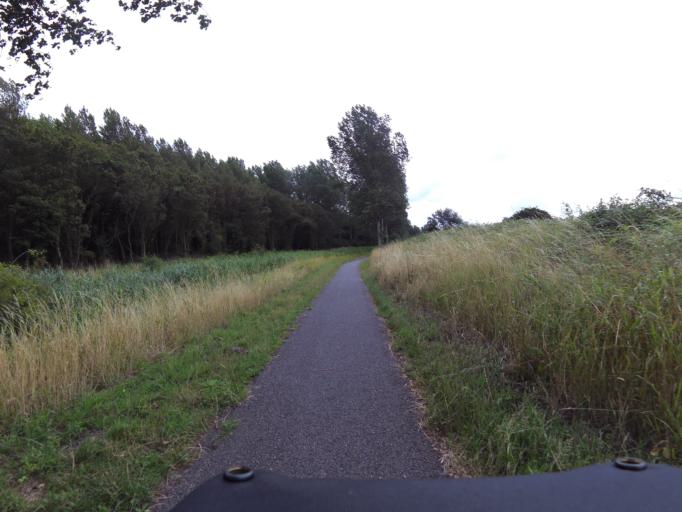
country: NL
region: South Holland
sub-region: Gemeente Goeree-Overflakkee
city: Goedereede
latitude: 51.8315
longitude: 4.0017
